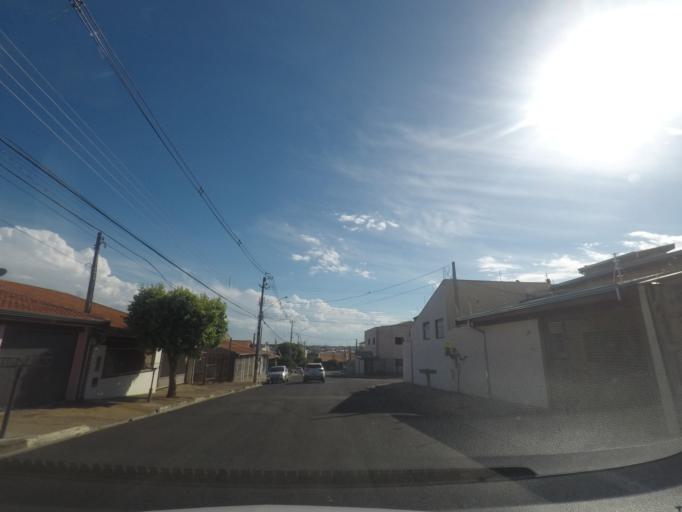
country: BR
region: Sao Paulo
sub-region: Sumare
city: Sumare
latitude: -22.8071
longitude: -47.2645
